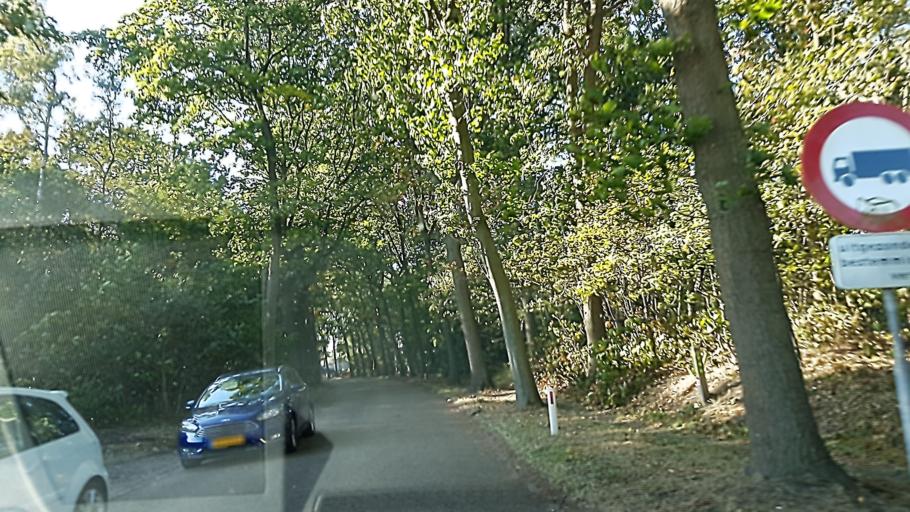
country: NL
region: North Brabant
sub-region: Gemeente Woensdrecht
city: Woensdrecht
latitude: 51.4344
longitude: 4.3860
